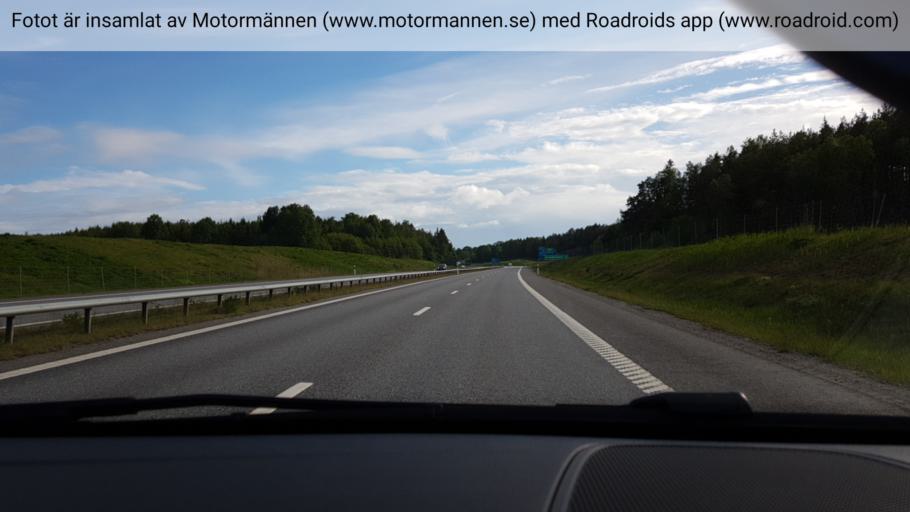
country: SE
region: Stockholm
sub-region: Nynashamns Kommun
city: Osmo
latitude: 58.9887
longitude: 17.9252
